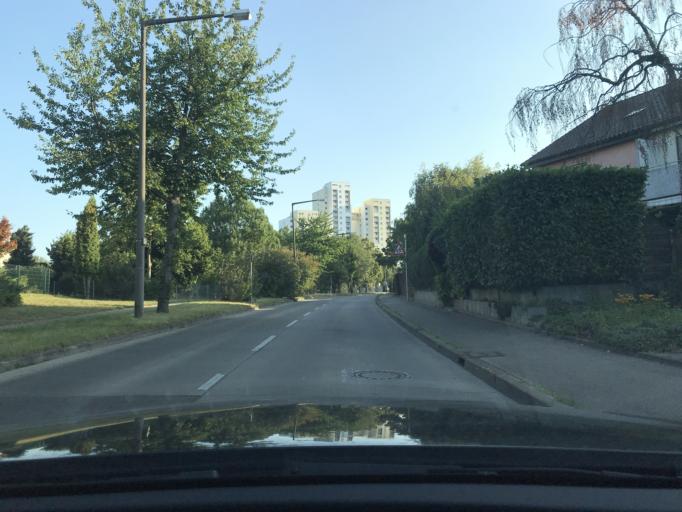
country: DE
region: Baden-Wuerttemberg
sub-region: Regierungsbezirk Stuttgart
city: Stuttgart Muehlhausen
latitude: 48.8341
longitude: 9.2384
